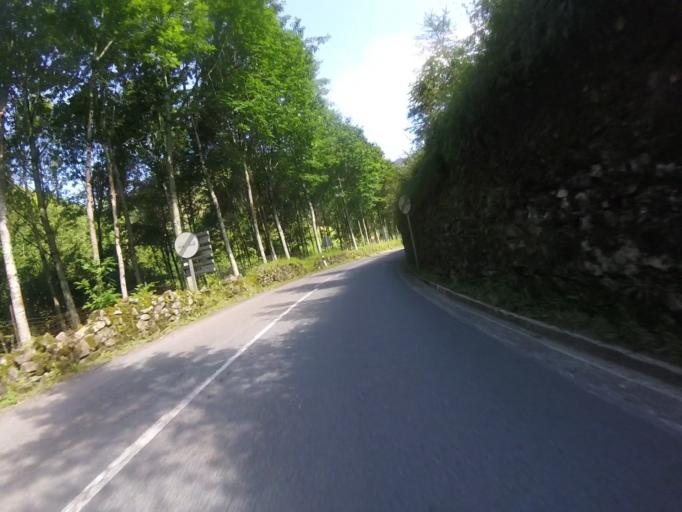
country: ES
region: Basque Country
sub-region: Provincia de Guipuzcoa
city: Beizama
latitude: 43.1055
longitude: -2.2420
